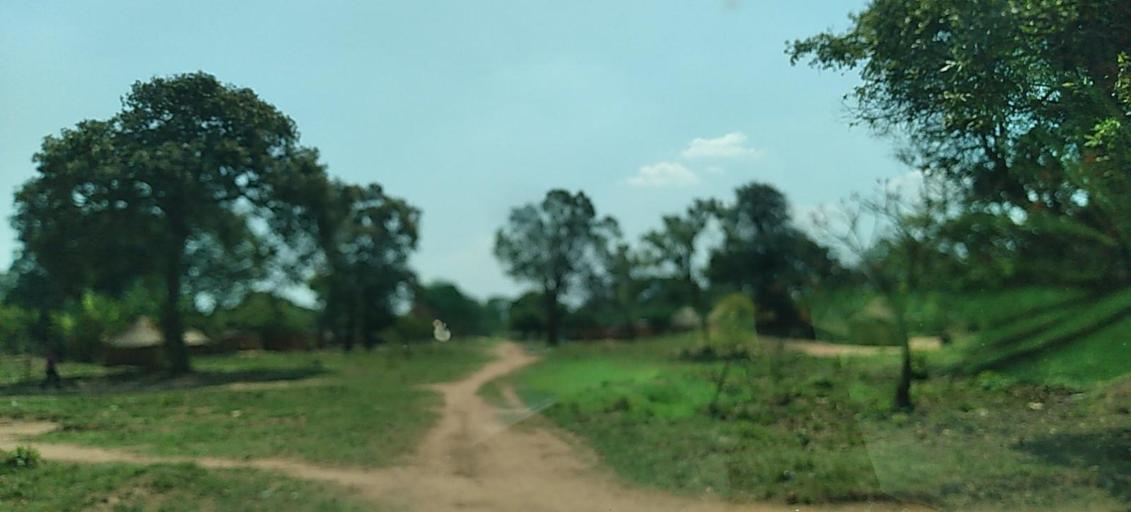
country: CD
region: Katanga
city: Kolwezi
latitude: -11.2791
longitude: 25.1268
